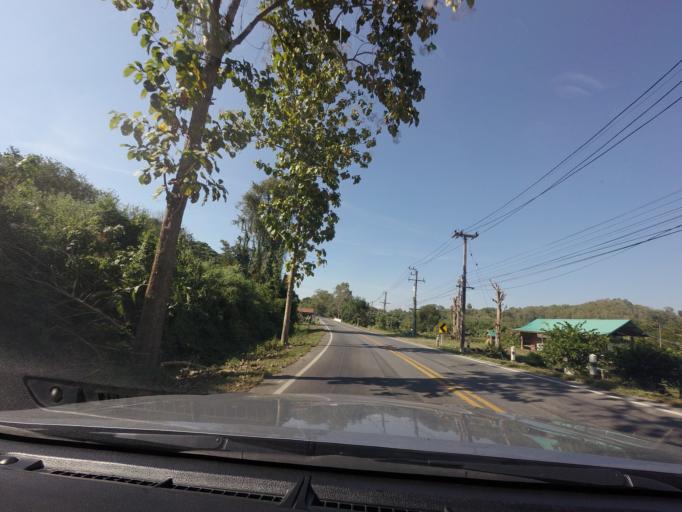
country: TH
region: Sukhothai
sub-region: Amphoe Si Satchanalai
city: Si Satchanalai
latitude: 17.6173
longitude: 99.7089
